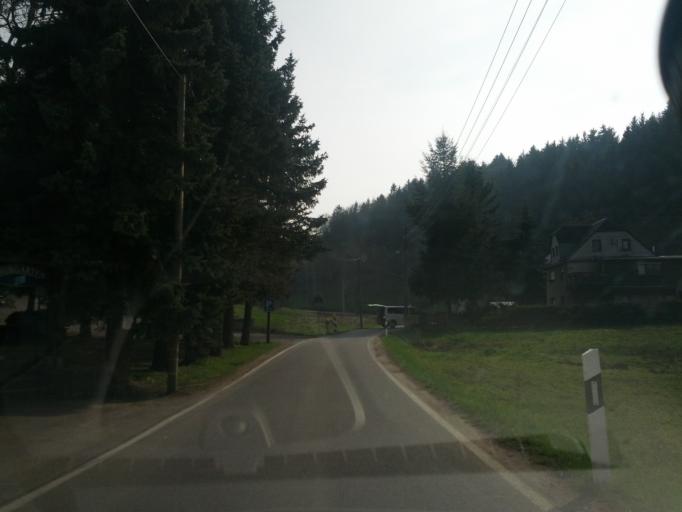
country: DE
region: Saxony
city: Kirchberg
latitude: 50.5902
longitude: 12.5165
